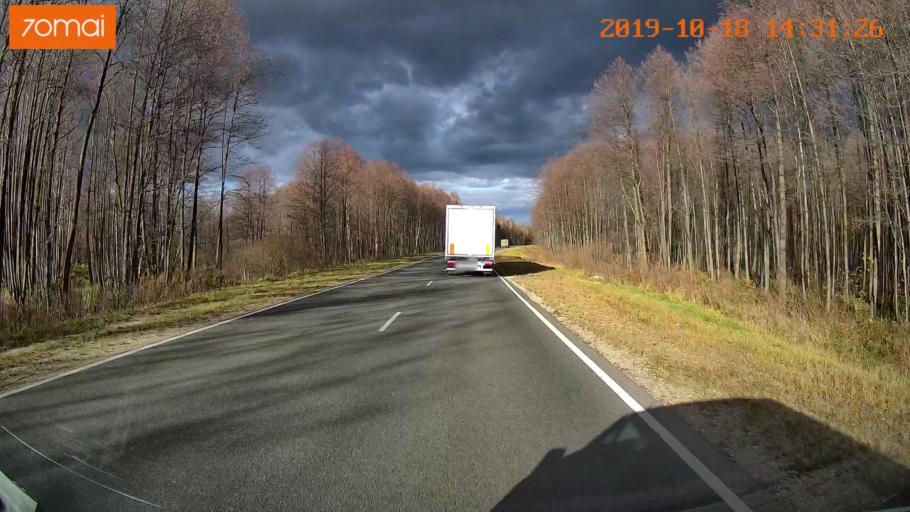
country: RU
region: Rjazan
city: Tuma
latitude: 55.1825
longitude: 40.5700
